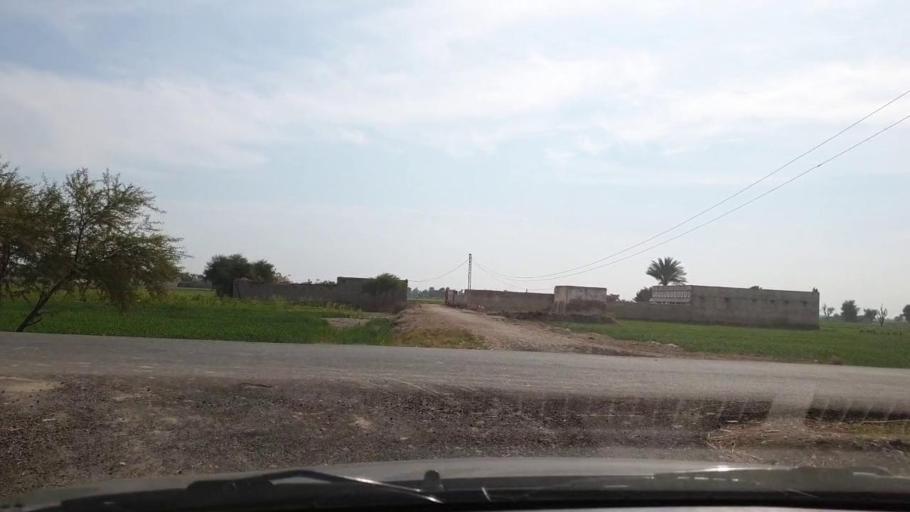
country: PK
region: Sindh
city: Shahpur Chakar
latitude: 26.2178
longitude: 68.6866
